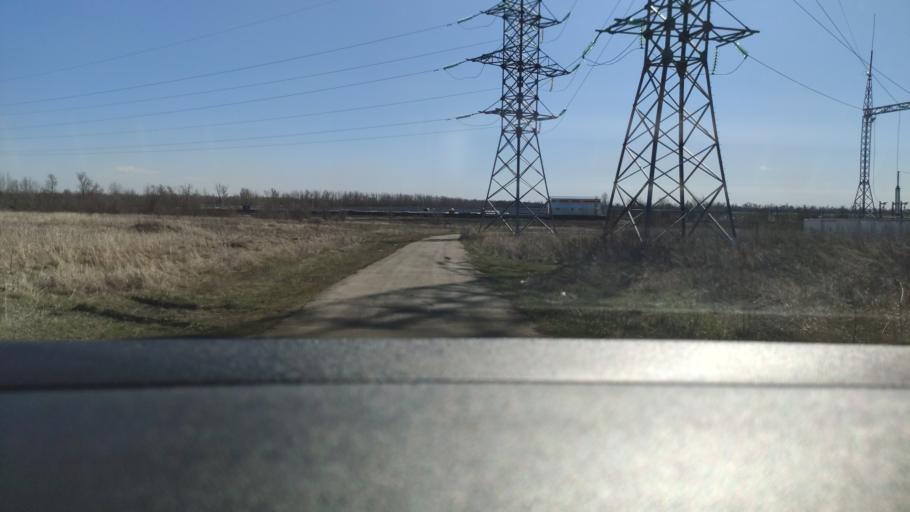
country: RU
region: Voronezj
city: Maslovka
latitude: 51.5030
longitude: 39.3055
